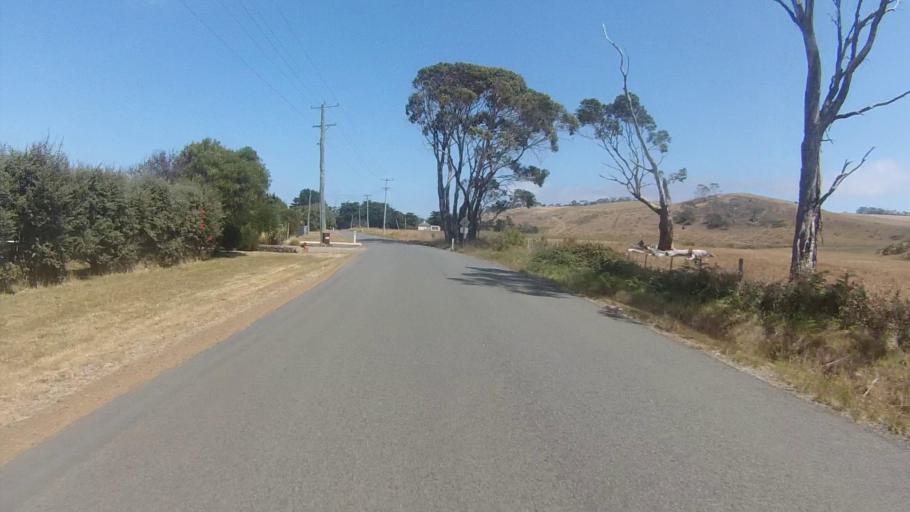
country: AU
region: Tasmania
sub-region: Sorell
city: Sorell
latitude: -42.8264
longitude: 147.8593
